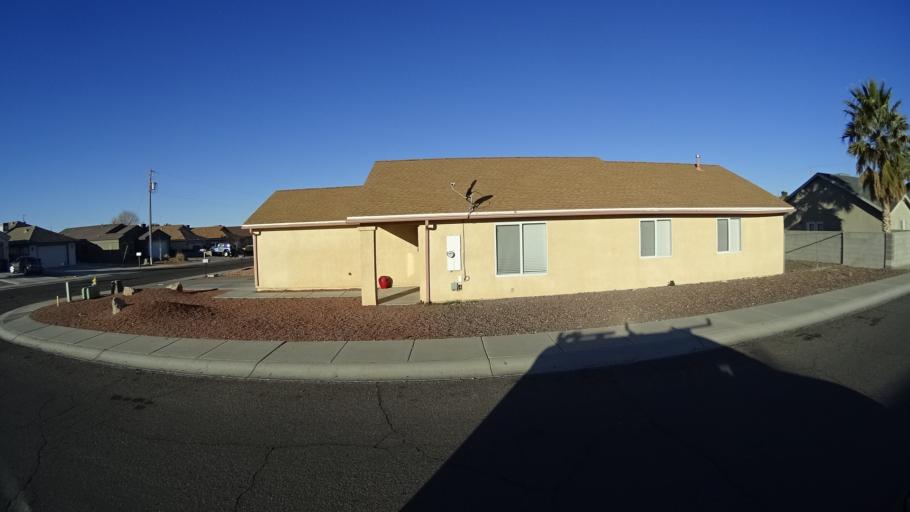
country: US
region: Arizona
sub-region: Mohave County
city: Kingman
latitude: 35.1974
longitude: -114.0137
